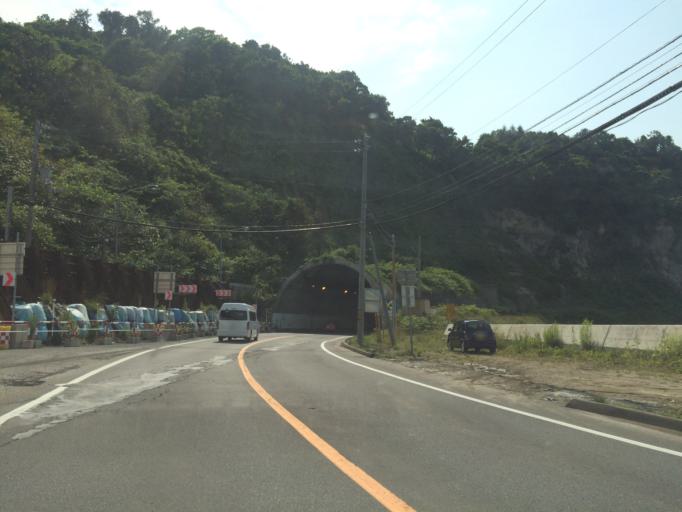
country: JP
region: Hokkaido
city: Otaru
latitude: 43.2080
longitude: 140.8927
